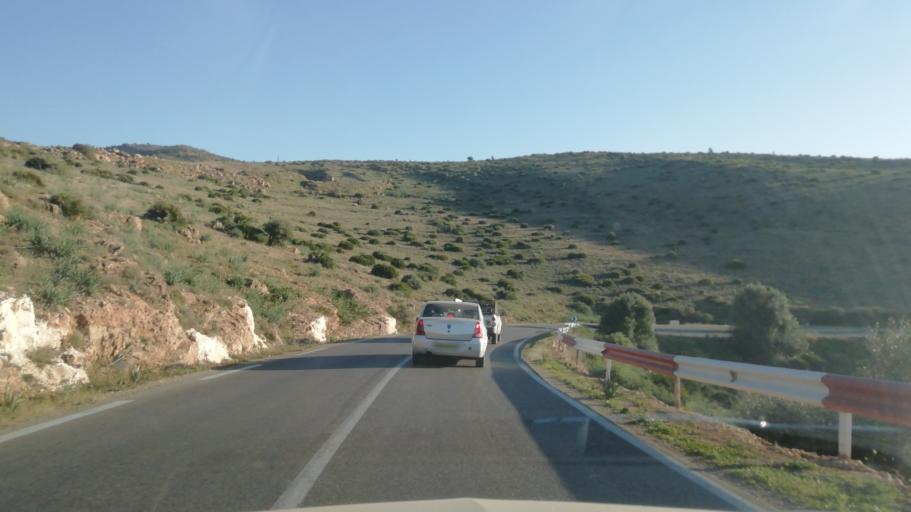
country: DZ
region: Tlemcen
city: Beni Mester
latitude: 34.8484
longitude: -1.4631
